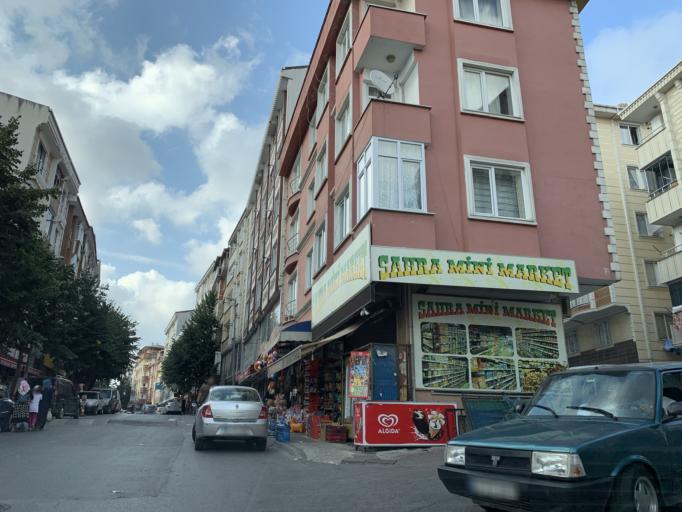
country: TR
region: Istanbul
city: Esenyurt
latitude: 41.0256
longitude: 28.6754
